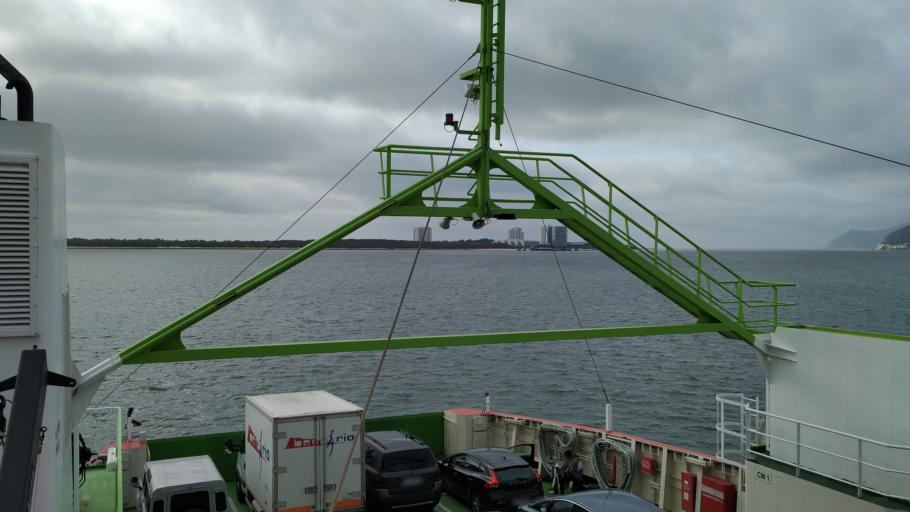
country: PT
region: Setubal
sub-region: Setubal
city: Setubal
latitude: 38.5052
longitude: -8.8882
